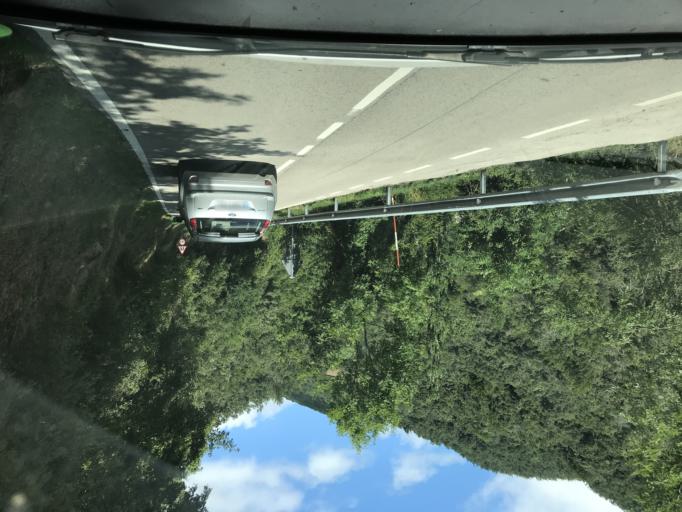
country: ES
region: Cantabria
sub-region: Provincia de Cantabria
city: Cabezon de Liebana
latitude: 43.0760
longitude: -4.4981
